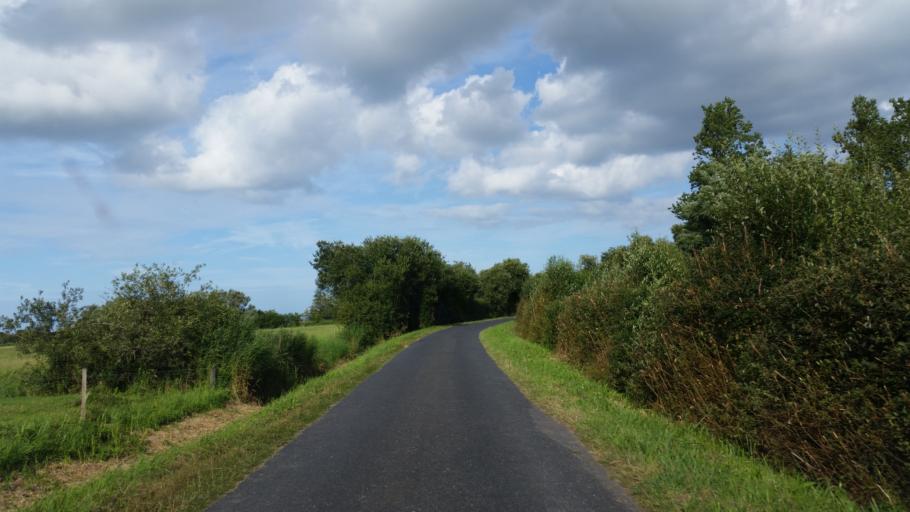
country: FR
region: Lower Normandy
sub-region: Departement de la Manche
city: Sainte-Mere-Eglise
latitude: 49.4517
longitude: -1.2487
